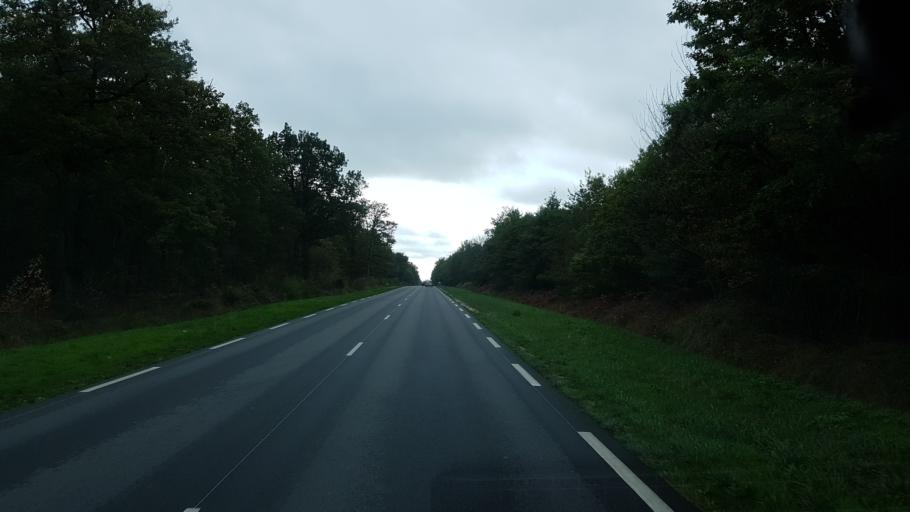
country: FR
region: Centre
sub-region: Departement du Loir-et-Cher
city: Theillay
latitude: 47.2646
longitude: 2.0598
